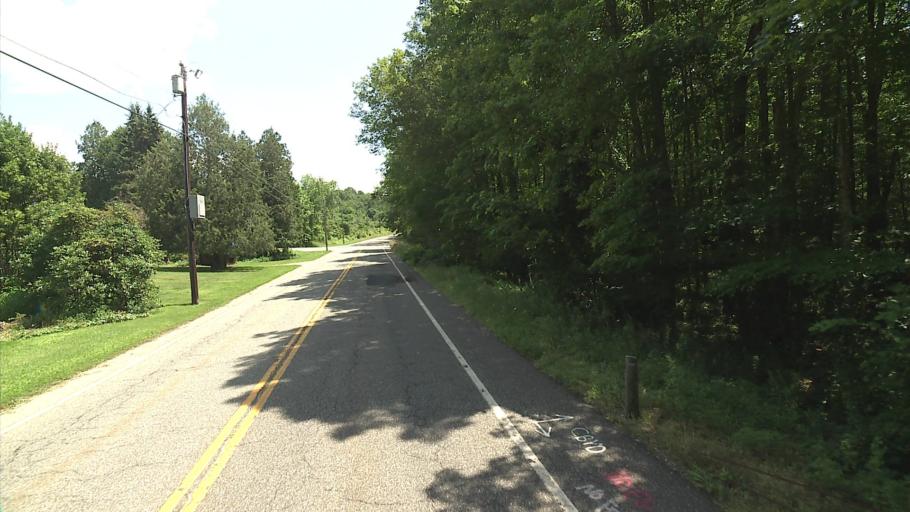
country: US
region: Connecticut
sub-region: Litchfield County
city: Litchfield
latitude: 41.8538
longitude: -73.3175
